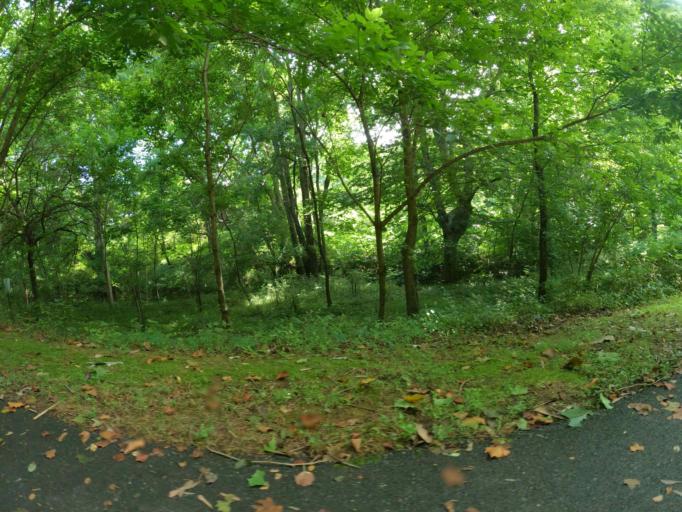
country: US
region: Maryland
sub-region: Frederick County
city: Brunswick
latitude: 39.3289
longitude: -77.6382
